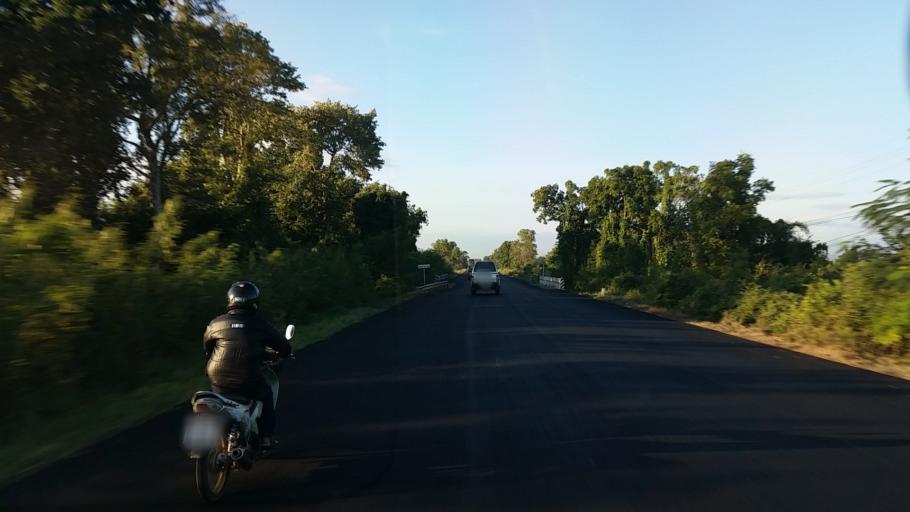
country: TH
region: Lop Buri
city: Chai Badan
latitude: 15.2370
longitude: 101.1617
